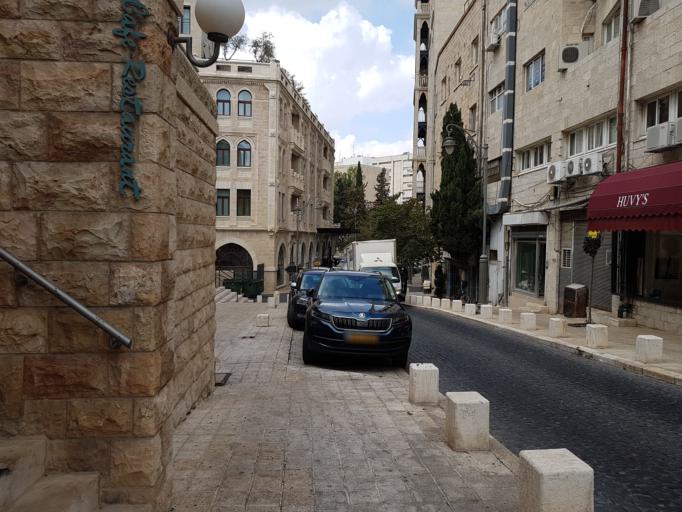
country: IL
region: Jerusalem
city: West Jerusalem
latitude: 31.7769
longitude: 35.2222
